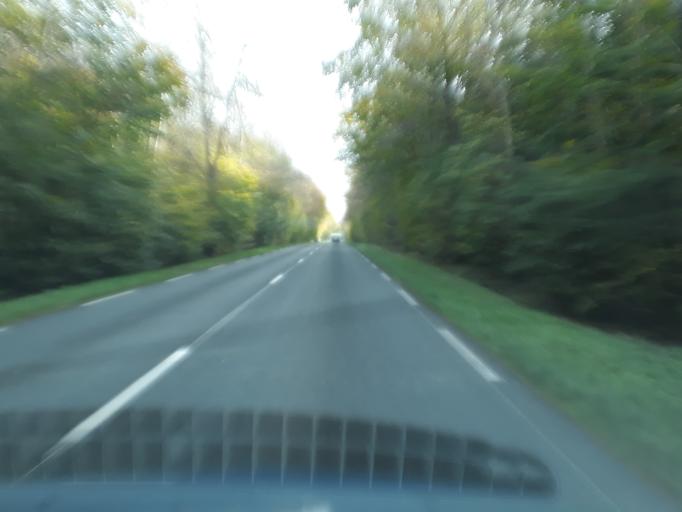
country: FR
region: Ile-de-France
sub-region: Departement de Seine-et-Marne
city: La Grande-Paroisse
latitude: 48.4185
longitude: 2.9069
